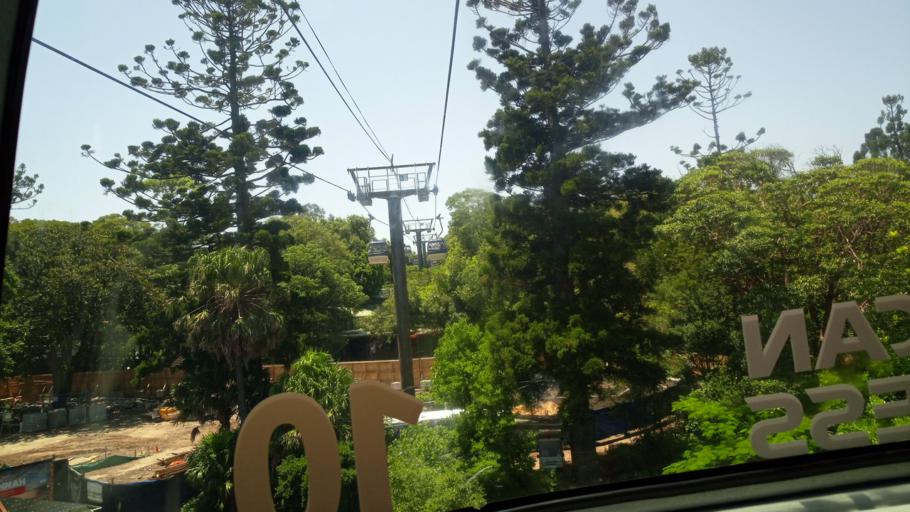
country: AU
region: New South Wales
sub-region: Mosman
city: Mosman
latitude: -33.8441
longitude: 151.2407
